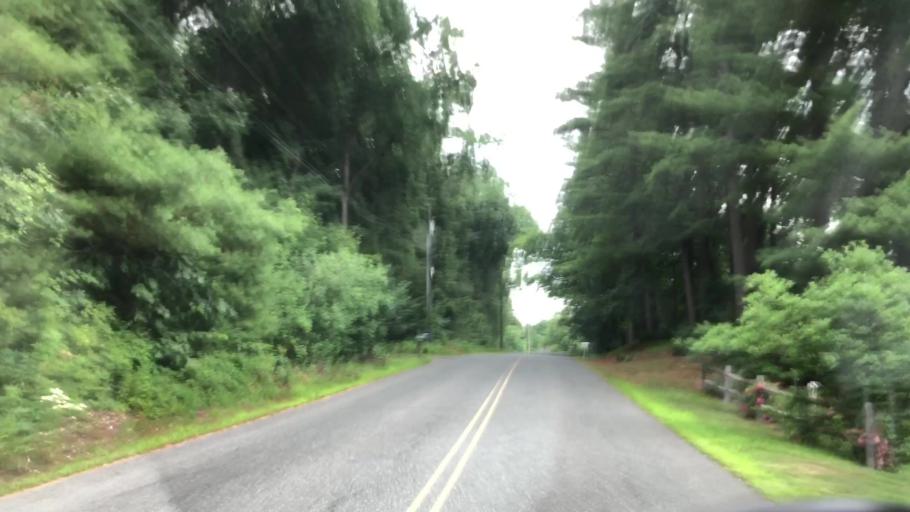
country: US
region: Massachusetts
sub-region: Hampshire County
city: Southampton
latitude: 42.2166
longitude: -72.6809
